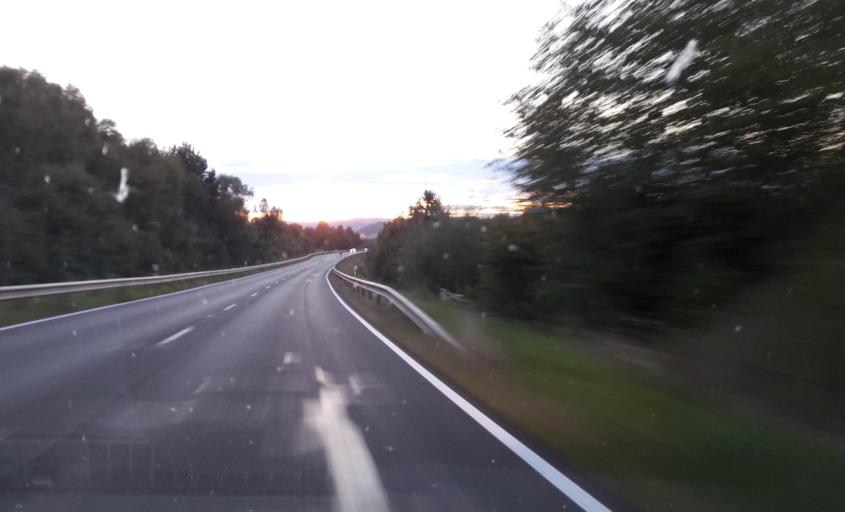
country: DE
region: Rheinland-Pfalz
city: Urzig
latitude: 49.9836
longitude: 6.9880
